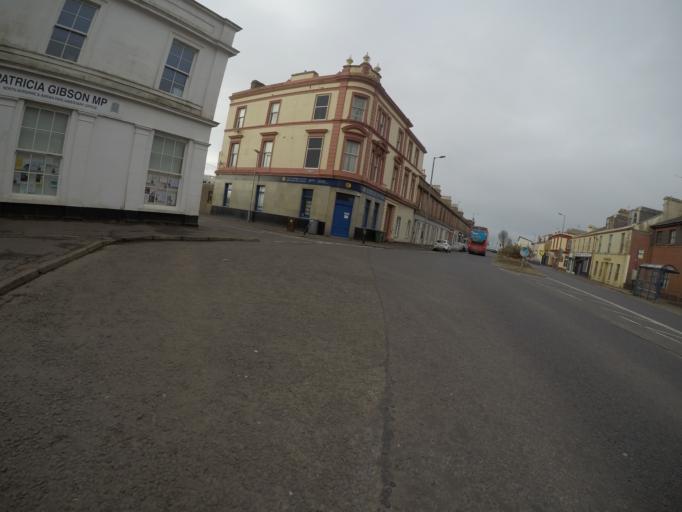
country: GB
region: Scotland
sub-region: North Ayrshire
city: Ardrossan
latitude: 55.6395
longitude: -4.8132
